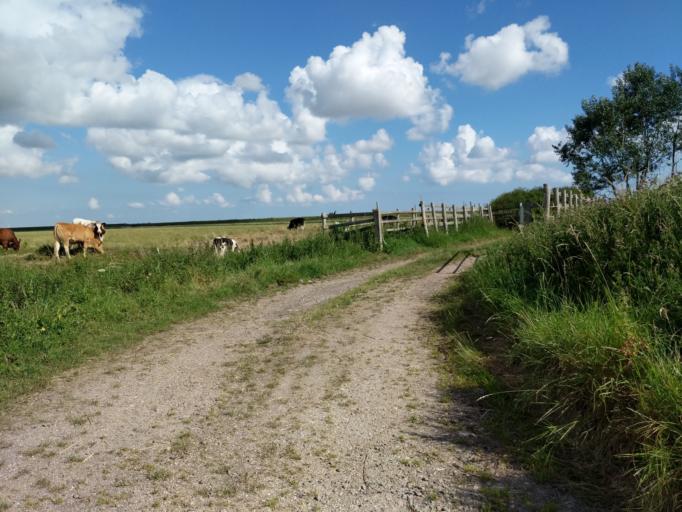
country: GB
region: England
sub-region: Kent
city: Dunkirk
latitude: 51.3422
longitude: 0.9572
